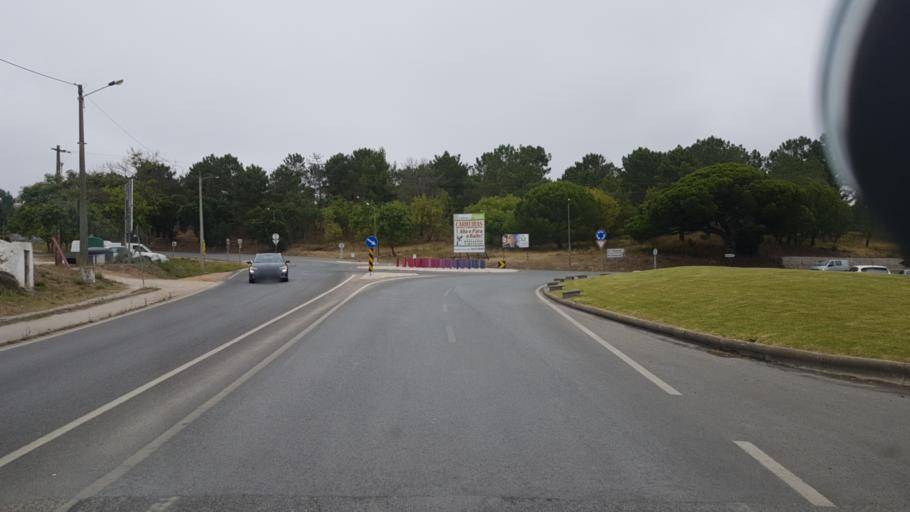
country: PT
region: Lisbon
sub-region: Torres Vedras
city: Torres Vedras
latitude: 39.1054
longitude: -9.2590
